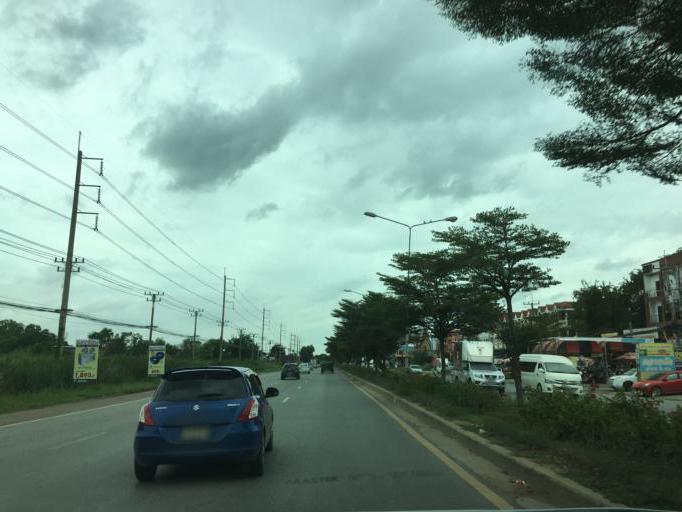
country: TH
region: Phra Nakhon Si Ayutthaya
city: Wang Noi
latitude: 14.2747
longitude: 100.6825
